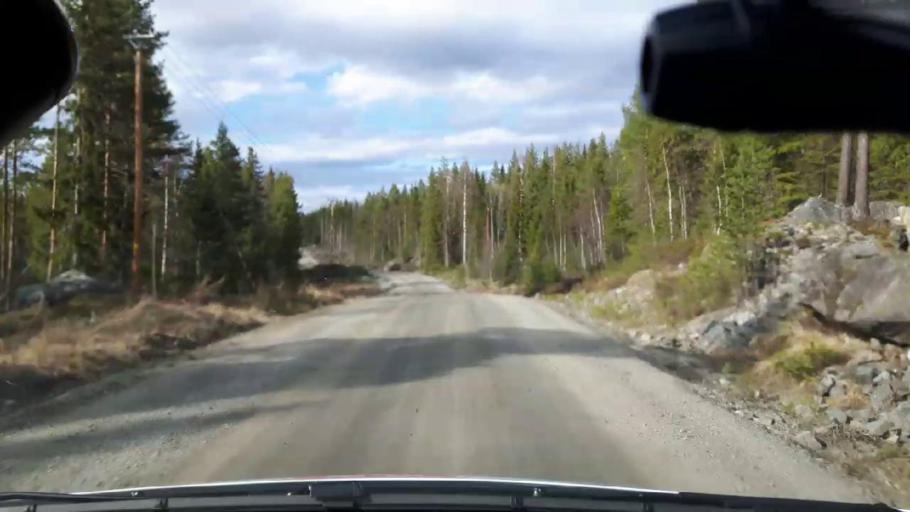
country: SE
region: Jaemtland
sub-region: Bergs Kommun
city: Hoverberg
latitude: 62.8725
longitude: 14.6662
